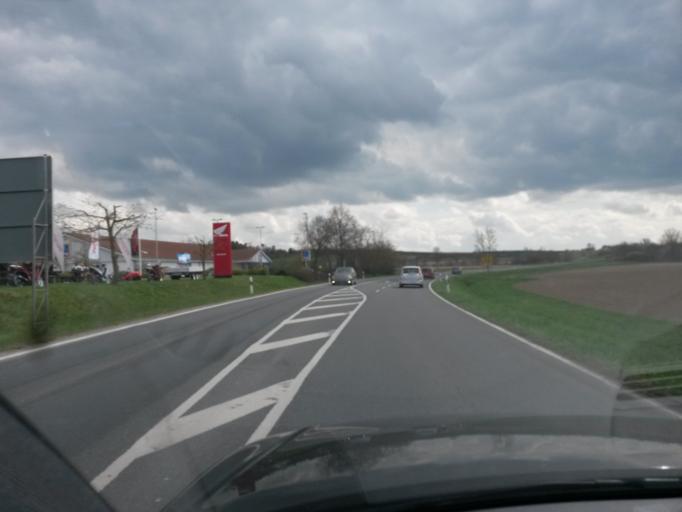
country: DE
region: Bavaria
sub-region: Regierungsbezirk Unterfranken
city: Volkach
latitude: 49.8569
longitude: 10.2291
